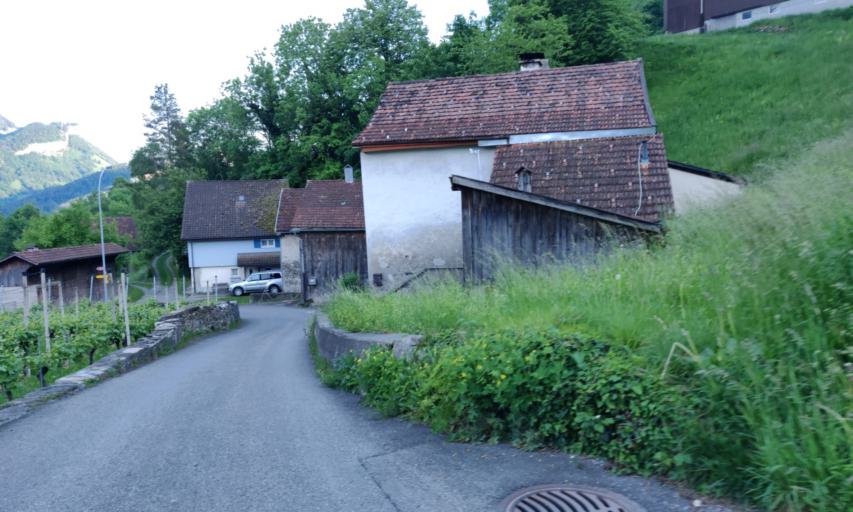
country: LI
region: Balzers
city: Balzers
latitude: 47.0742
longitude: 9.4723
